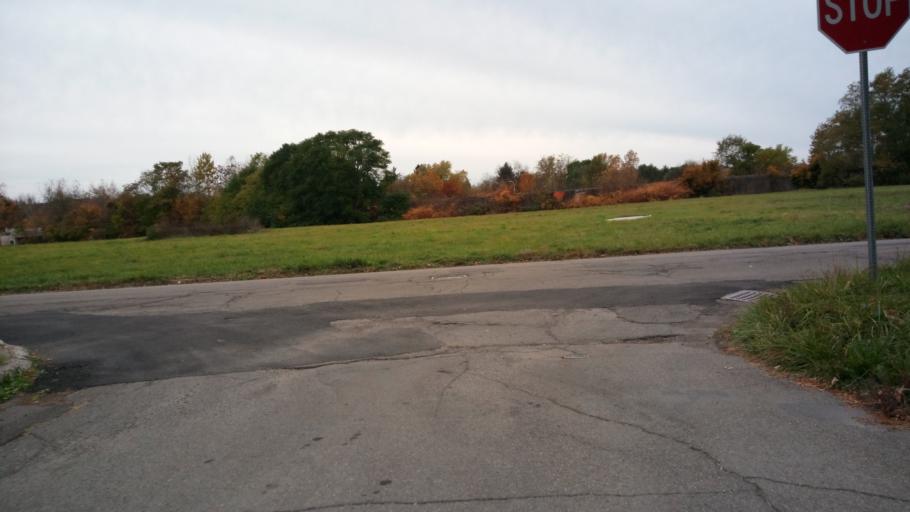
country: US
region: New York
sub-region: Chemung County
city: Elmira
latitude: 42.0787
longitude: -76.7983
